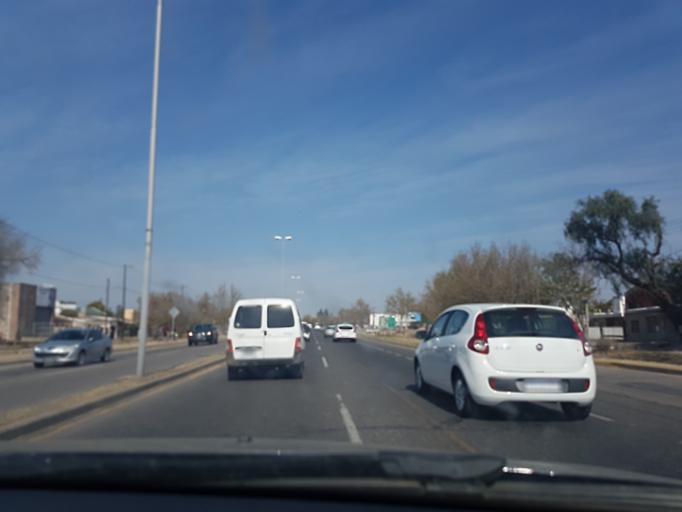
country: AR
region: Cordoba
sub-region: Departamento de Capital
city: Cordoba
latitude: -31.4804
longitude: -64.2404
